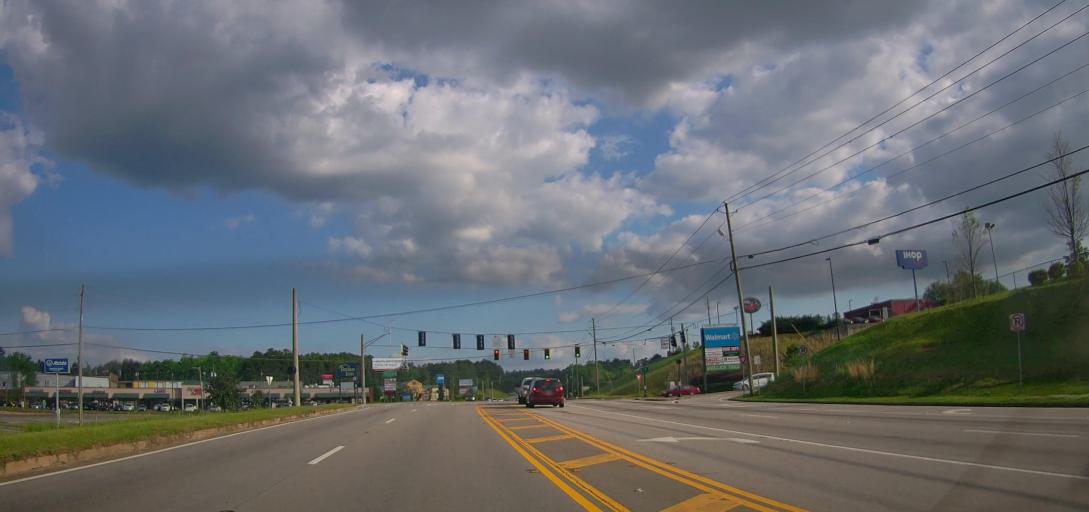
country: US
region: Georgia
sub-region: Baldwin County
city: Milledgeville
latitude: 33.1198
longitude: -83.2615
